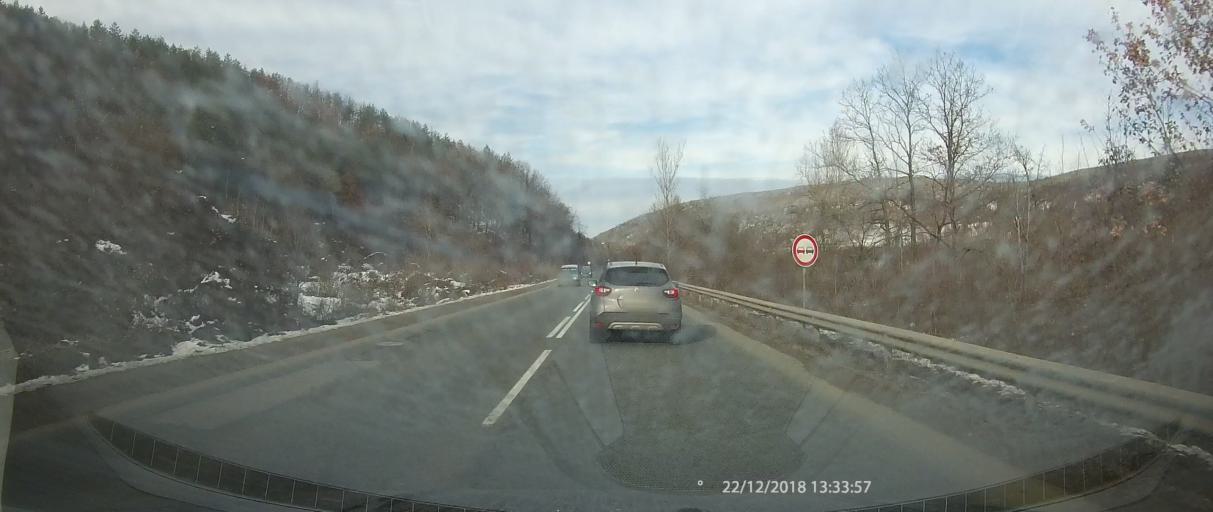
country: BG
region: Lovech
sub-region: Obshtina Lukovit
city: Lukovit
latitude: 43.1155
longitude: 24.1487
